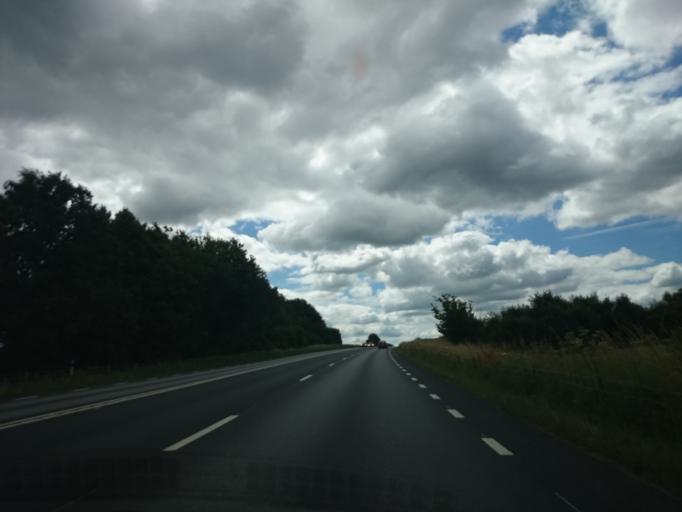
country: SE
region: Skane
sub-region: Kristianstads Kommun
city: Degeberga
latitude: 55.7960
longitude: 14.1470
